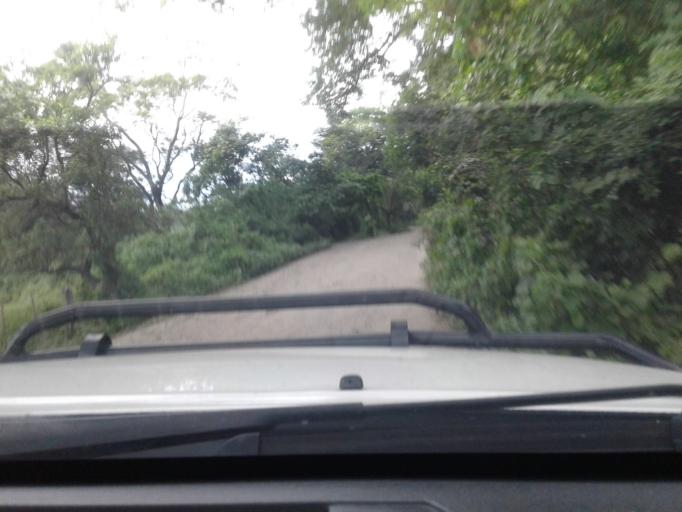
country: NI
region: Matagalpa
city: Ciudad Dario
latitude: 12.9085
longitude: -86.1993
